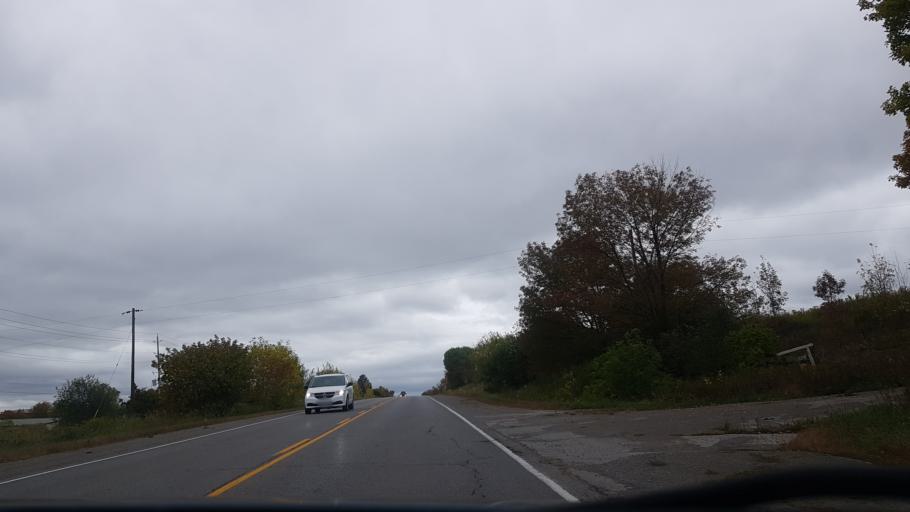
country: CA
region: Ontario
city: Peterborough
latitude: 44.2580
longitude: -78.3908
